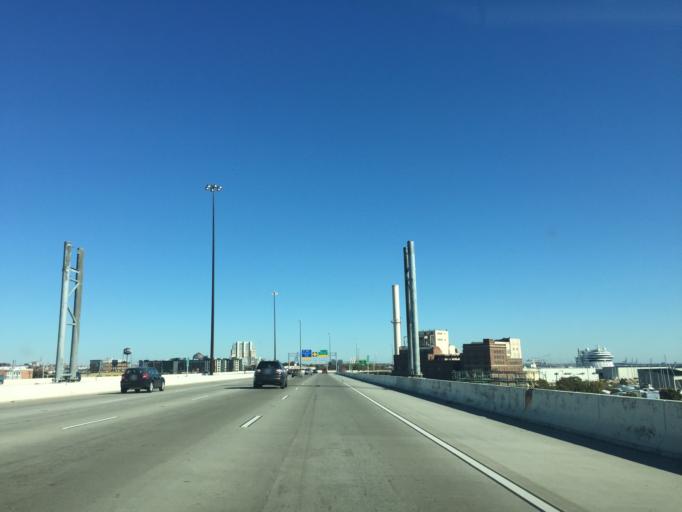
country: US
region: Maryland
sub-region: City of Baltimore
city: Baltimore
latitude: 39.2668
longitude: -76.6091
